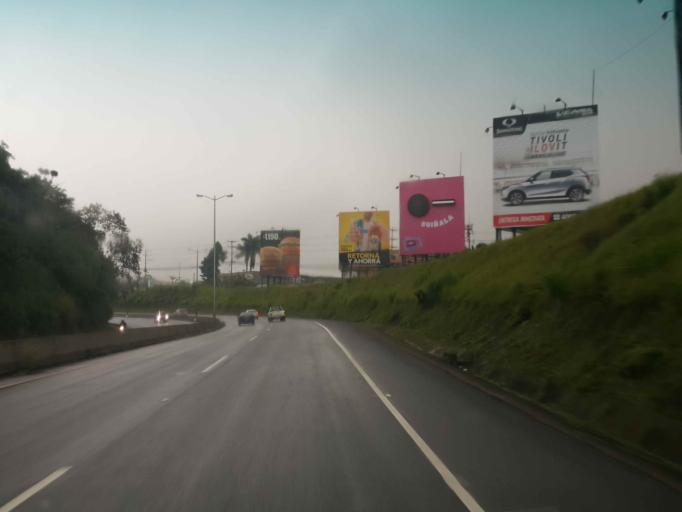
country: CR
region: San Jose
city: San Rafael
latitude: 9.9349
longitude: -84.1125
